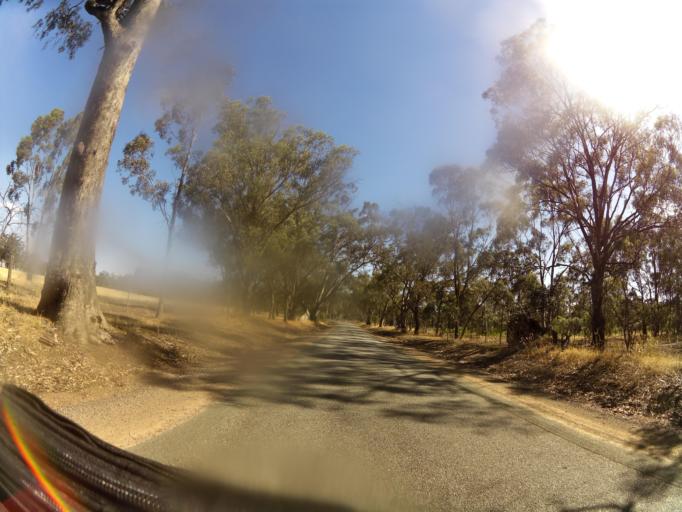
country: AU
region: Victoria
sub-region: Campaspe
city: Kyabram
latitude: -36.8753
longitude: 145.0856
